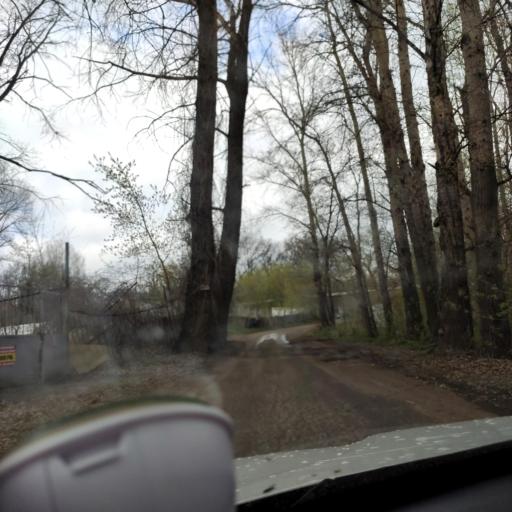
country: RU
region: Samara
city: Novokuybyshevsk
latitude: 53.1410
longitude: 49.9702
